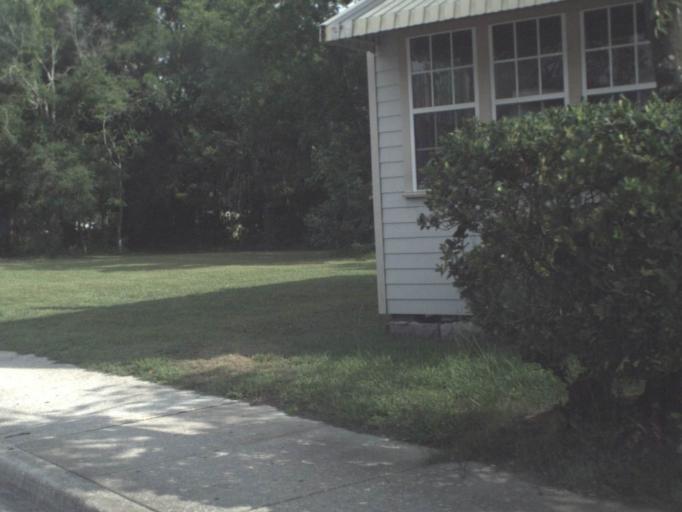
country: US
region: Florida
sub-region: Duval County
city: Jacksonville
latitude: 30.3426
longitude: -81.6801
